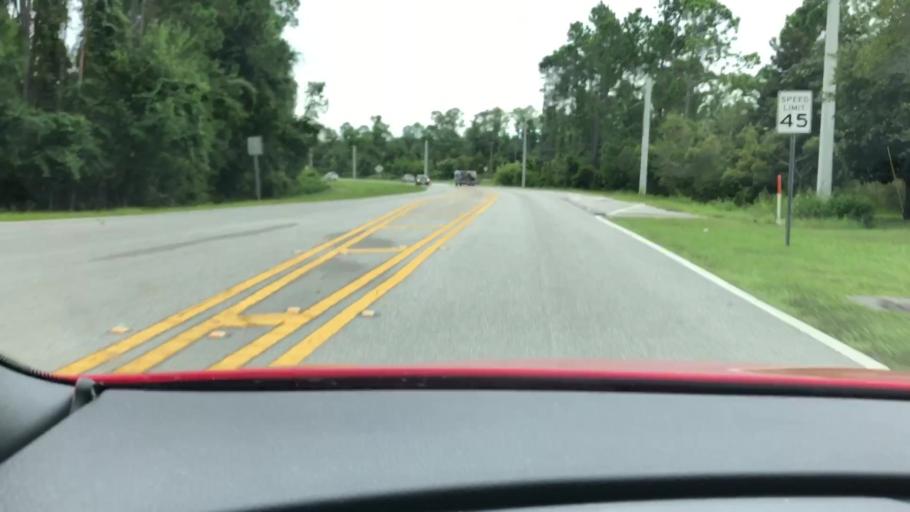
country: US
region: Florida
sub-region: Flagler County
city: Palm Coast
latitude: 29.5508
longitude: -81.2136
